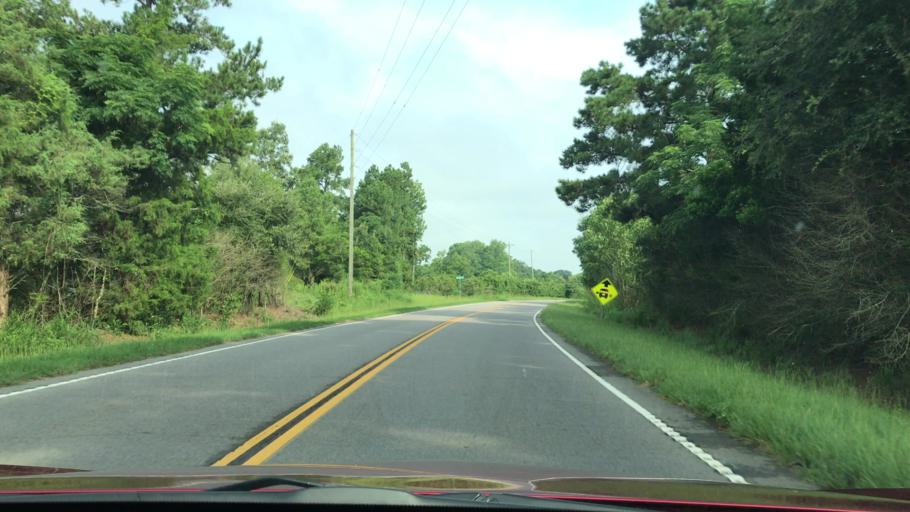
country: US
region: South Carolina
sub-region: Lexington County
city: Batesburg-Leesville
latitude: 33.6906
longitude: -81.4712
